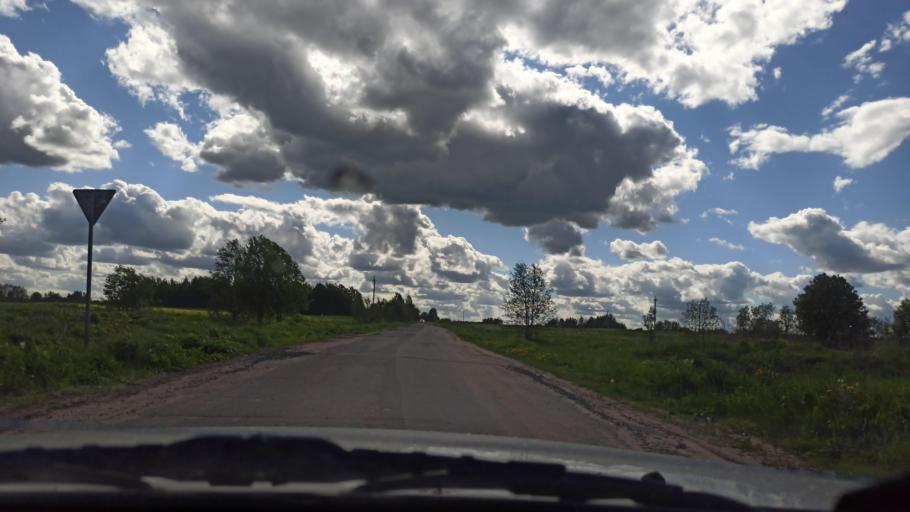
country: RU
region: Vologda
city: Molochnoye
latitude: 59.3850
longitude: 39.7329
